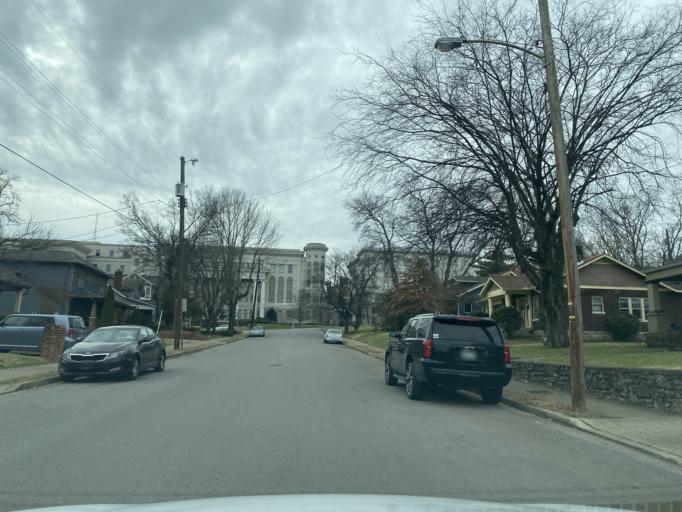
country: US
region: Tennessee
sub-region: Davidson County
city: Nashville
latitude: 36.1372
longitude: -86.7931
